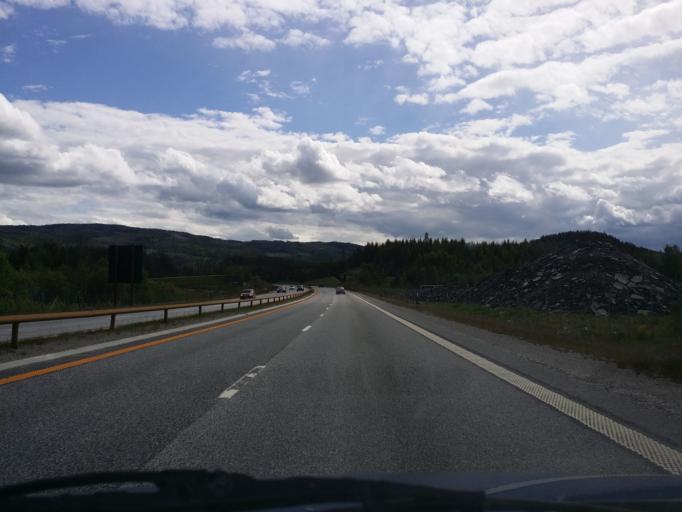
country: NO
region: Hedmark
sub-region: Stange
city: Stange
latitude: 60.6240
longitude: 11.2992
